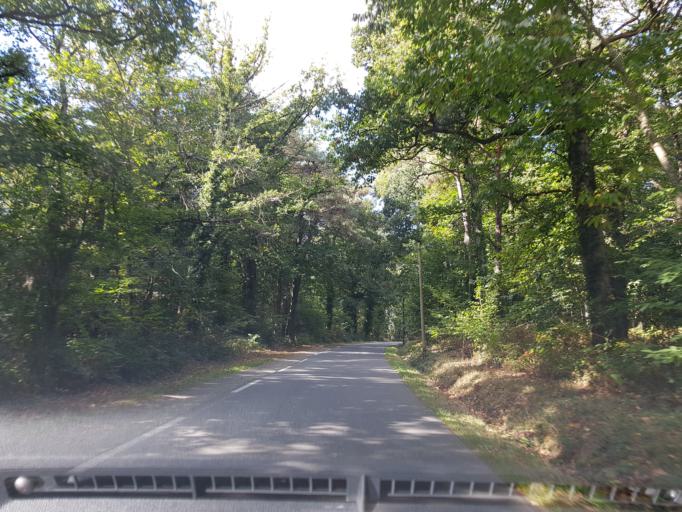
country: FR
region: Brittany
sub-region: Departement des Cotes-d'Armor
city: Pledran
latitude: 48.4600
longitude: -2.7255
